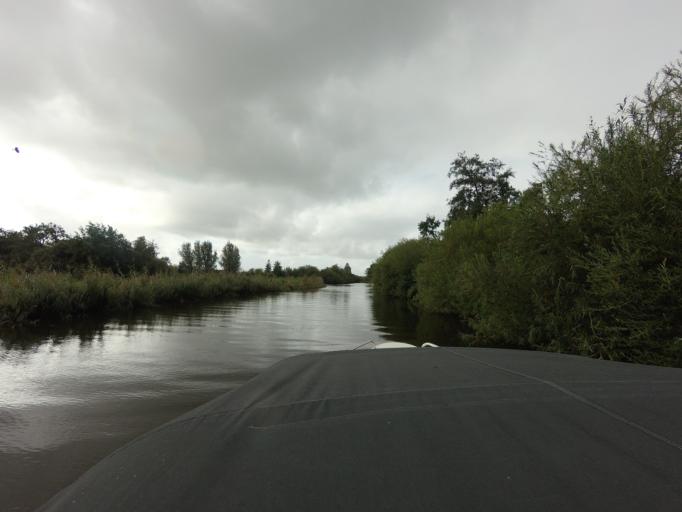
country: NL
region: Friesland
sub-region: Gemeente Boarnsterhim
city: Warten
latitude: 53.1377
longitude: 5.9100
